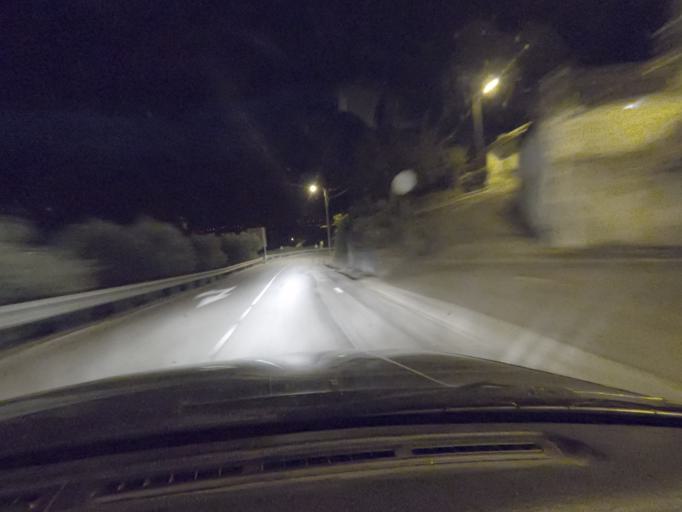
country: PT
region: Vila Real
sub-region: Santa Marta de Penaguiao
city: Santa Marta de Penaguiao
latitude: 41.2245
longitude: -7.8188
